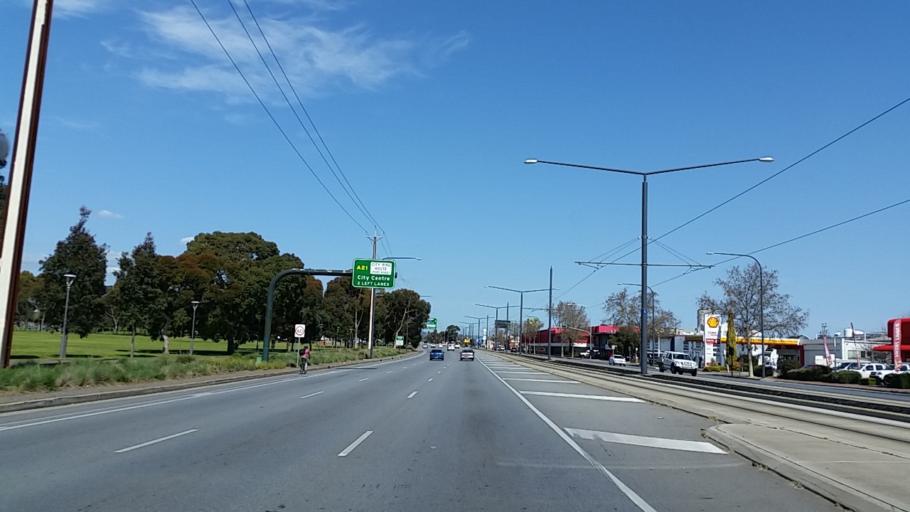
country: AU
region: South Australia
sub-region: City of West Torrens
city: Thebarton
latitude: -34.9139
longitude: 138.5780
